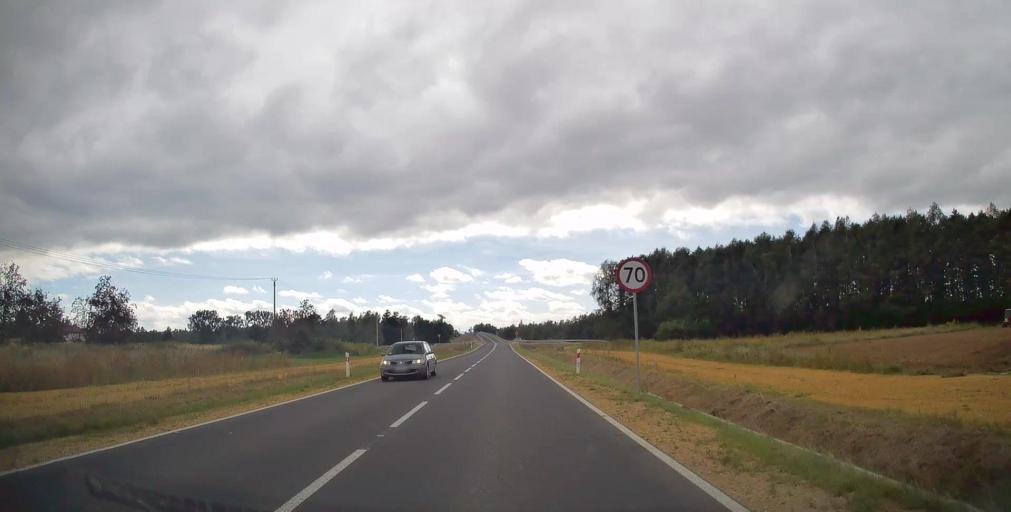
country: PL
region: Lesser Poland Voivodeship
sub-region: Powiat oswiecimski
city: Zator
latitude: 50.0075
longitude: 19.4240
